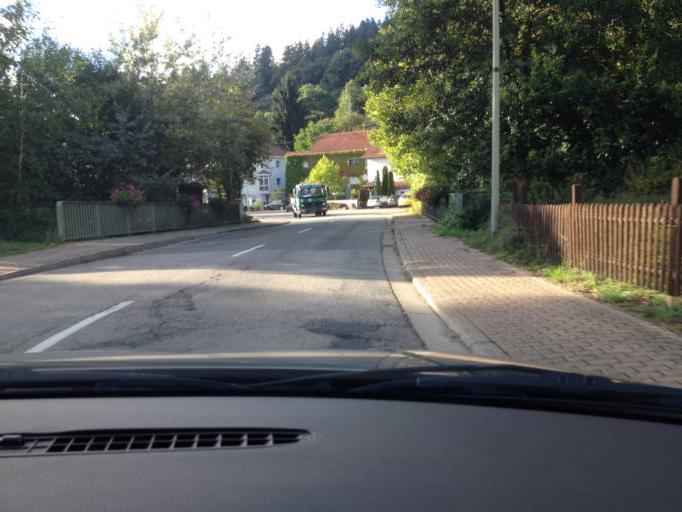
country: DE
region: Saarland
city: Marpingen
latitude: 49.4336
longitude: 7.0365
